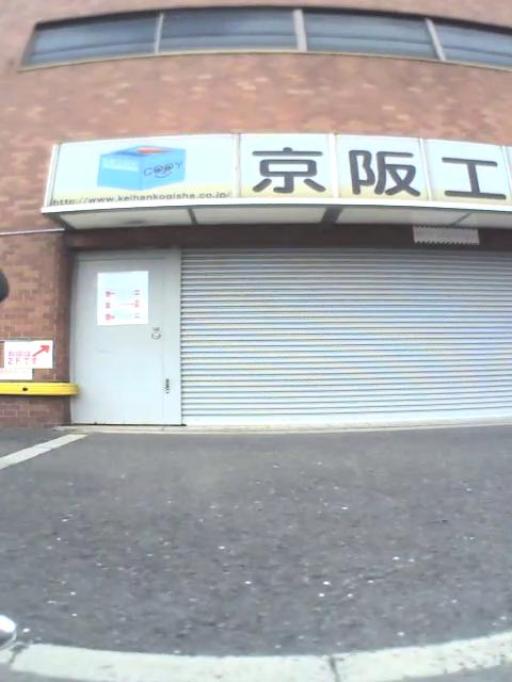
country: JP
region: Osaka
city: Neyagawa
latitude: 34.7607
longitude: 135.6282
